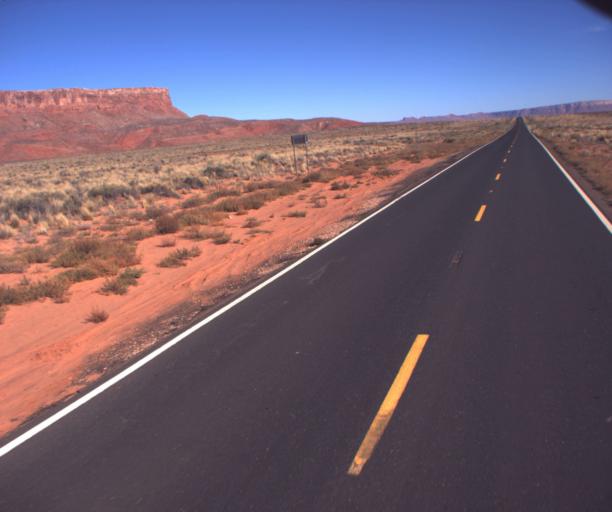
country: US
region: Arizona
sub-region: Coconino County
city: Page
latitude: 36.6956
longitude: -111.9072
